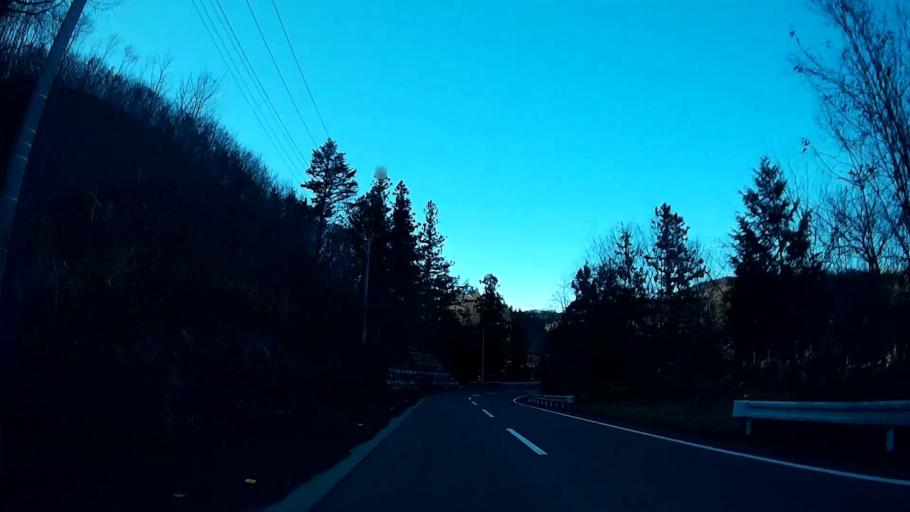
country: JP
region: Saitama
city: Chichibu
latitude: 36.0375
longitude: 139.0117
